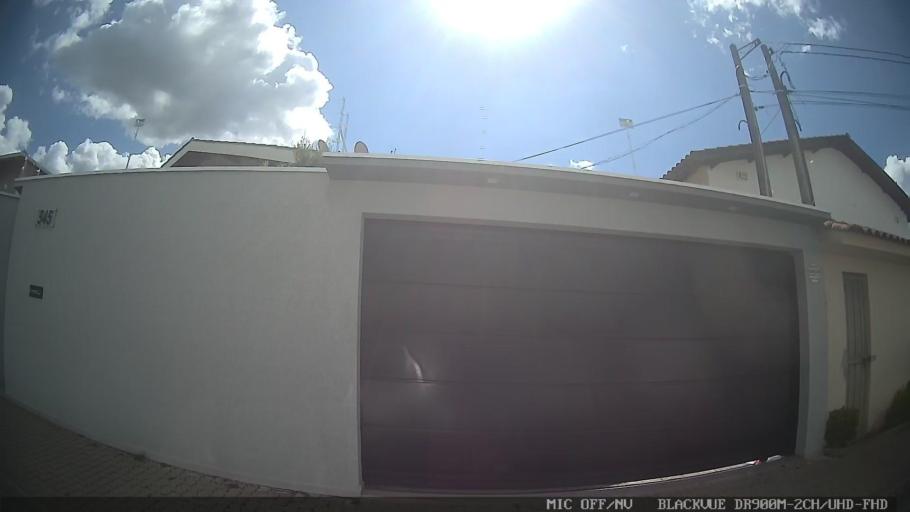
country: BR
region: Sao Paulo
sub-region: Atibaia
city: Atibaia
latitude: -23.1435
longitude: -46.5613
